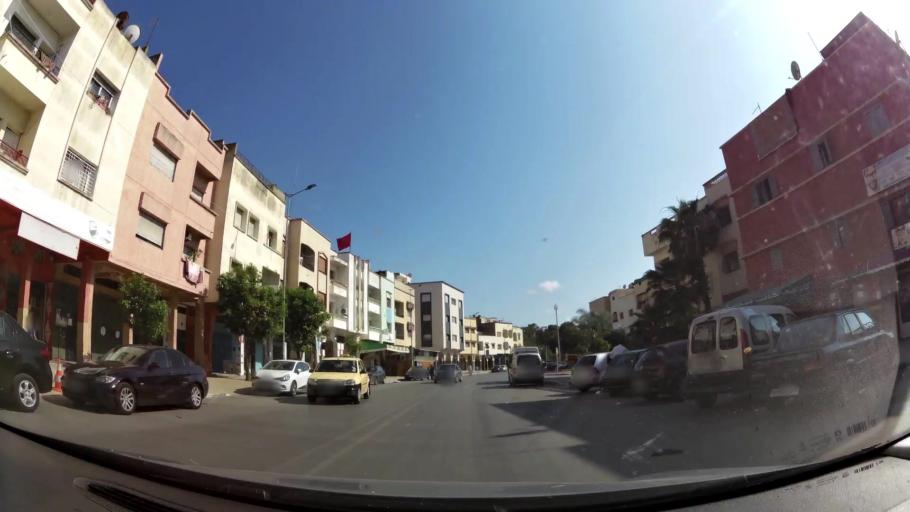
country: MA
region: Rabat-Sale-Zemmour-Zaer
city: Sale
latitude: 34.0419
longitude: -6.7797
